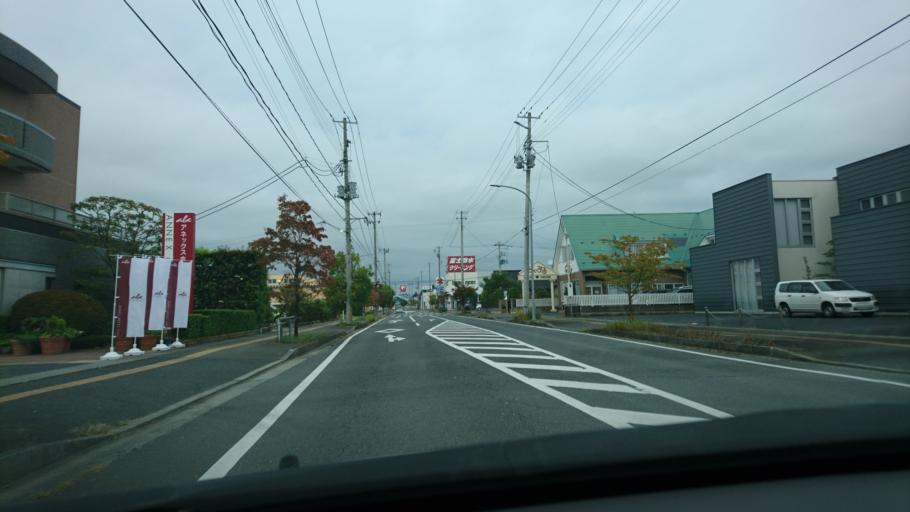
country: JP
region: Iwate
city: Ichinoseki
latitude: 38.7697
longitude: 141.1231
